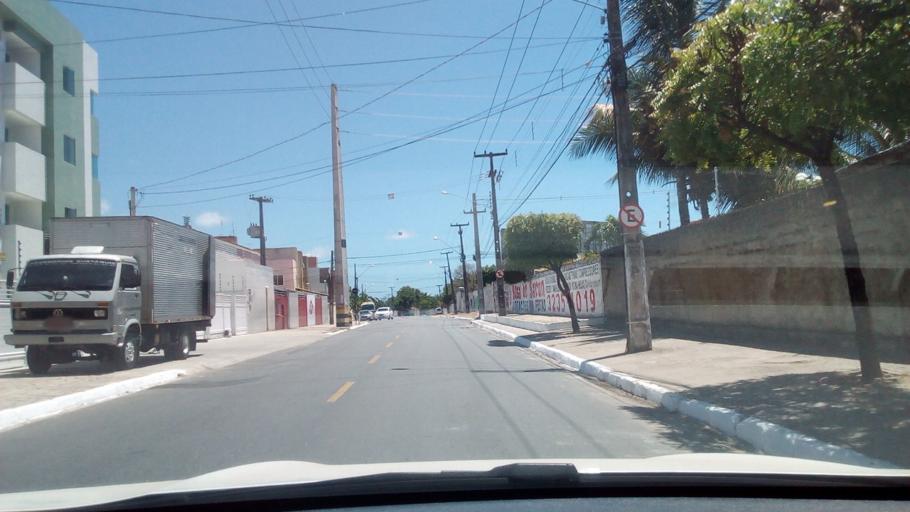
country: BR
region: Paraiba
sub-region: Joao Pessoa
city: Joao Pessoa
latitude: -7.1596
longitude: -34.8367
